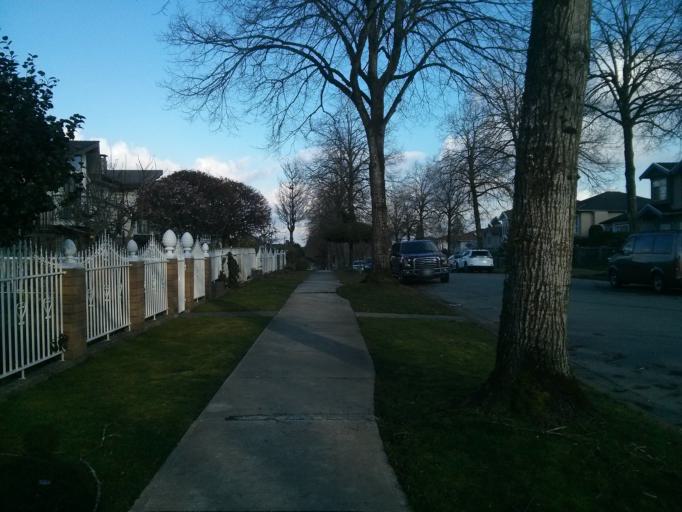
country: CA
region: British Columbia
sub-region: Fraser Valley Regional District
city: North Vancouver
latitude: 49.2454
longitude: -123.0321
